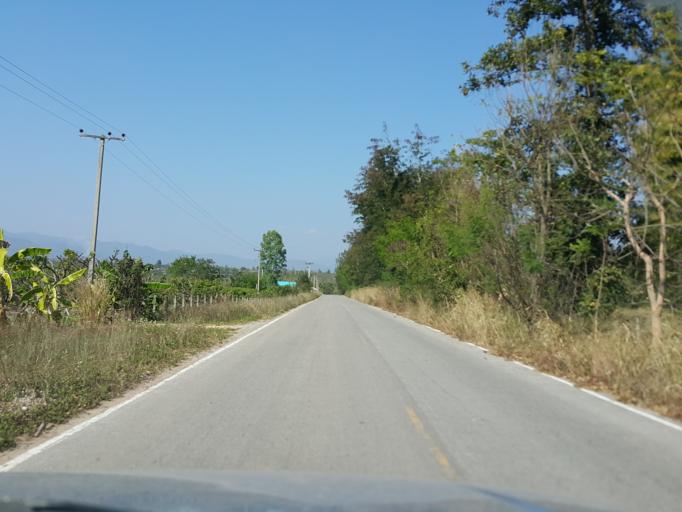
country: TH
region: Chiang Mai
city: Mae Wang
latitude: 18.5484
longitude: 98.7964
